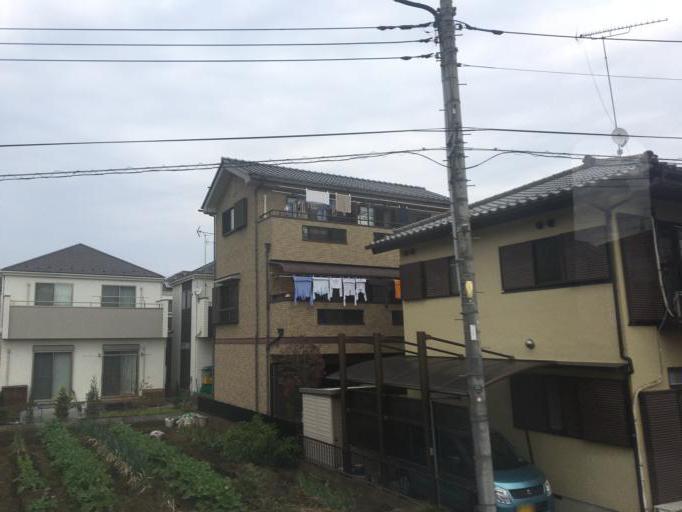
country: JP
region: Saitama
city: Hanno
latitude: 35.8472
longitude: 139.3281
